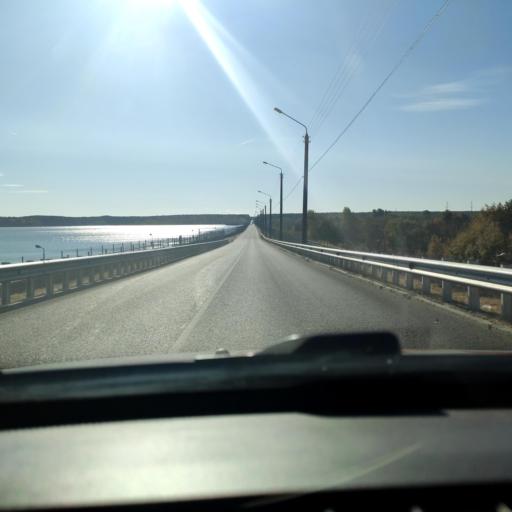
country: RU
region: Voronezj
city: Shilovo
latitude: 51.5494
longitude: 39.1359
